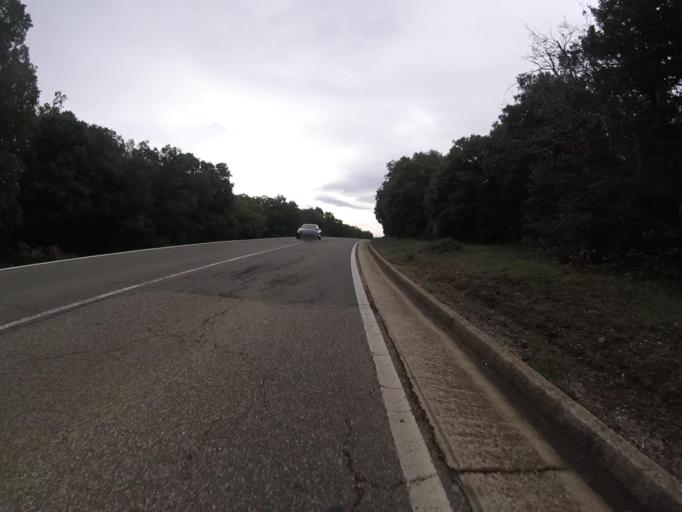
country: ES
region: Navarre
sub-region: Provincia de Navarra
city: Lezaun
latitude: 42.7573
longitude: -2.0118
